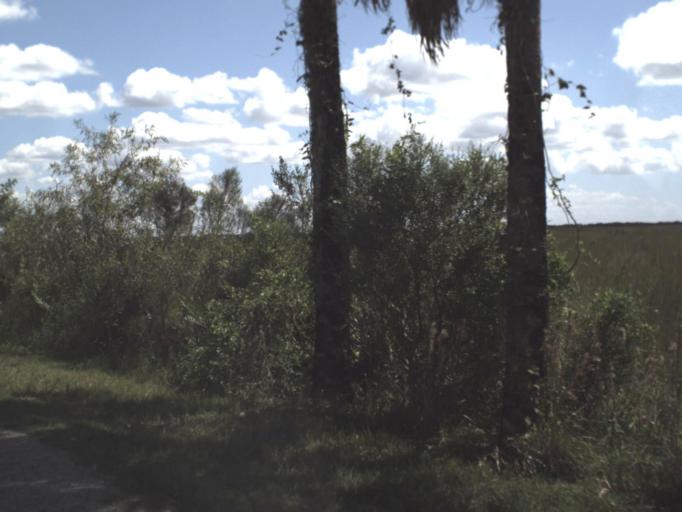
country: US
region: Florida
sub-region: Collier County
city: Marco
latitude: 25.9250
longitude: -81.4229
